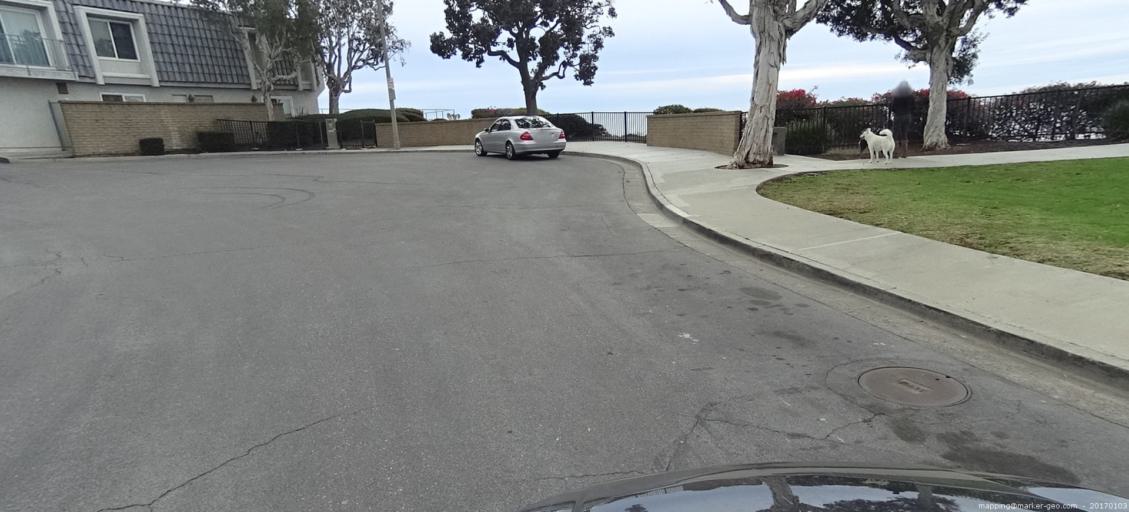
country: US
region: California
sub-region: Orange County
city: Dana Point
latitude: 33.4620
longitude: -117.6772
